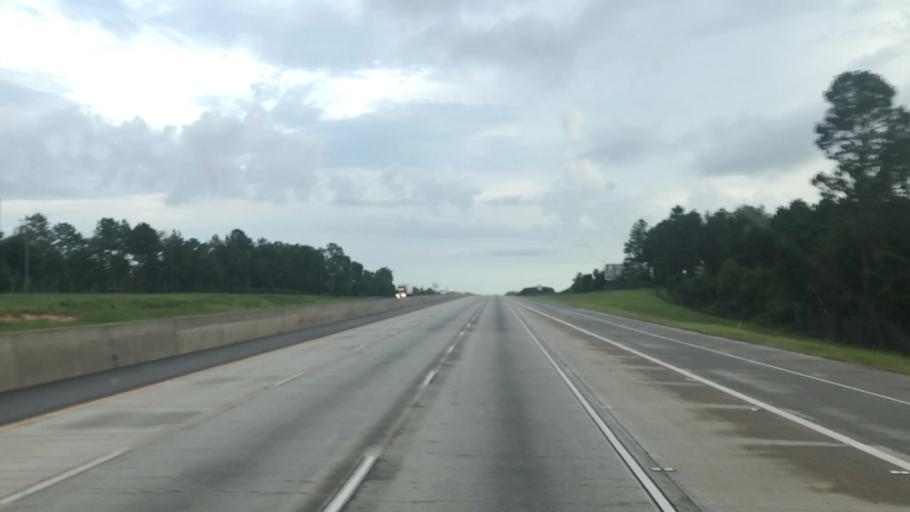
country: US
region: Georgia
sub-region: Tift County
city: Unionville
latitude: 31.3506
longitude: -83.4882
